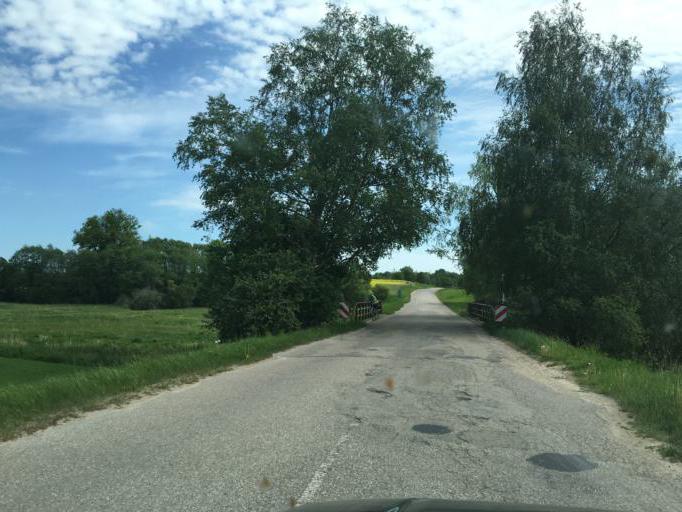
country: LV
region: Talsu Rajons
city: Valdemarpils
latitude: 57.3862
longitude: 22.5378
